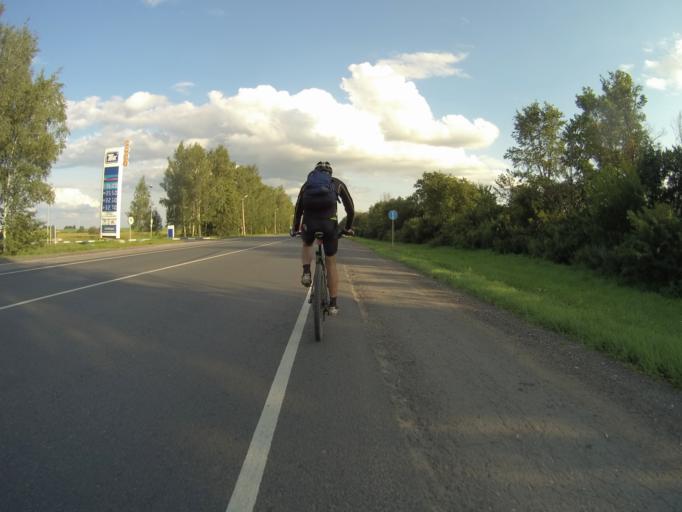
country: RU
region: Vladimir
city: Suzdal'
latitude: 56.3728
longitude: 40.4615
